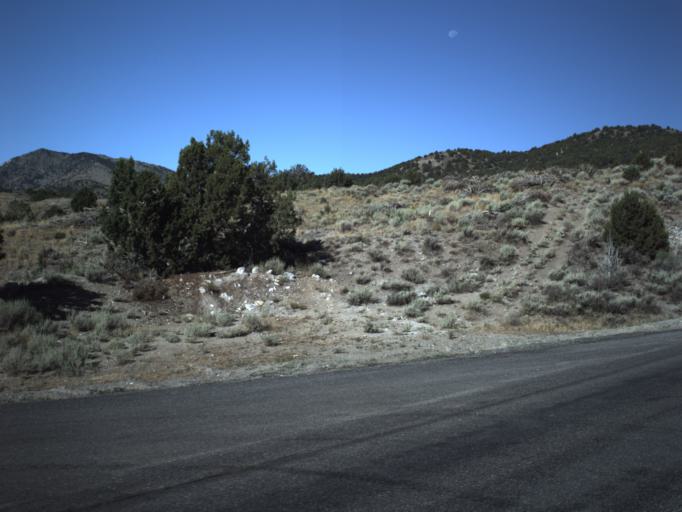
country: US
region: Utah
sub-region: Utah County
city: Genola
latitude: 39.9700
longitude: -112.0605
